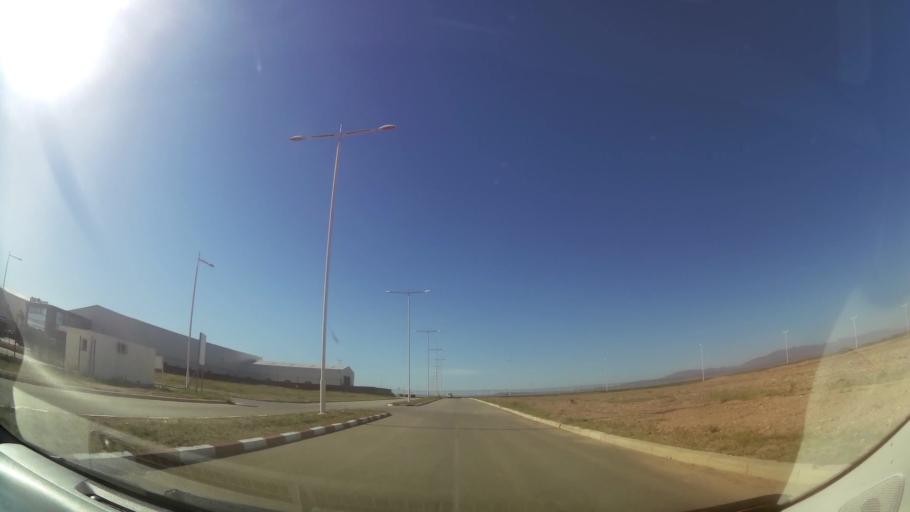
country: MA
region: Oriental
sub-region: Oujda-Angad
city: Oujda
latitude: 34.7711
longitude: -1.9296
